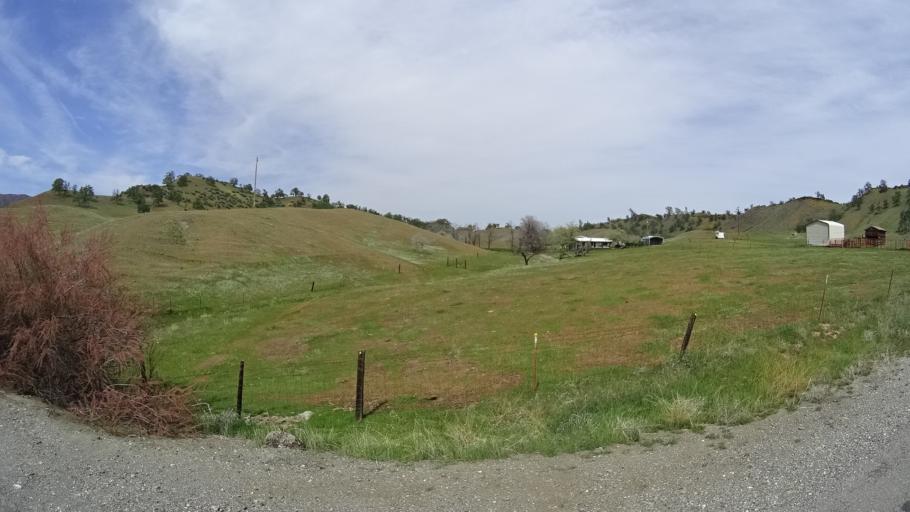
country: US
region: California
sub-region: Glenn County
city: Willows
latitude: 39.6157
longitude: -122.5877
